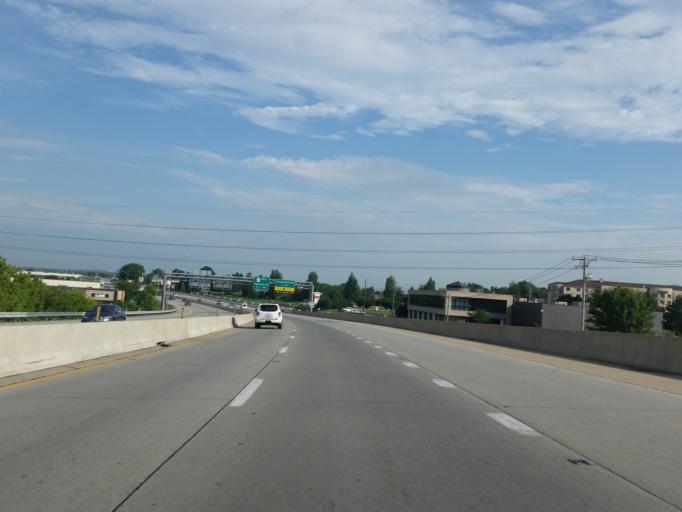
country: US
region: Pennsylvania
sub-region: Lancaster County
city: Lampeter
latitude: 40.0457
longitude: -76.2486
